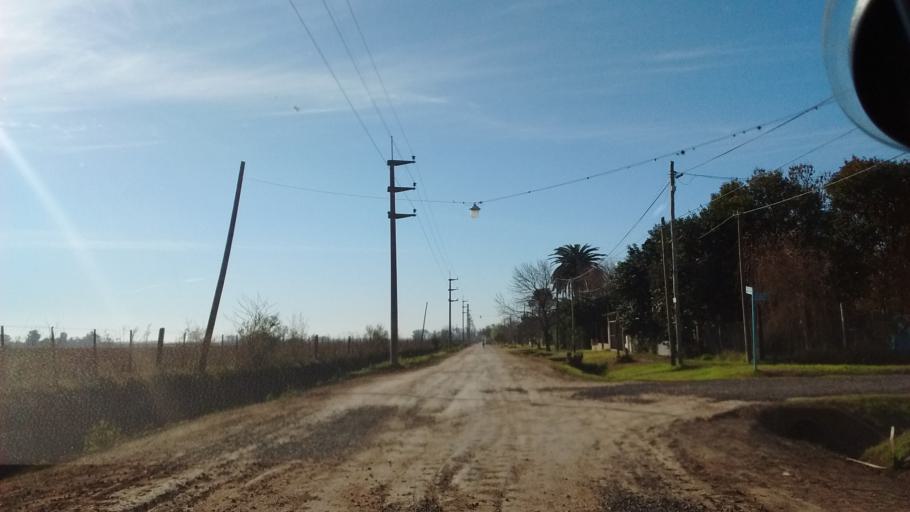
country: AR
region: Santa Fe
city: Funes
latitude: -32.9102
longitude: -60.8160
